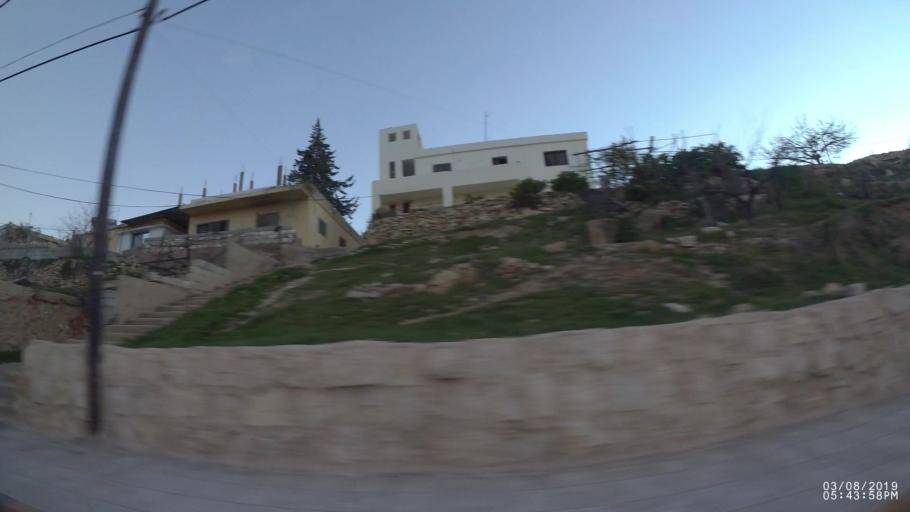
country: JO
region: Ma'an
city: Petra
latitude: 30.3119
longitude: 35.4795
